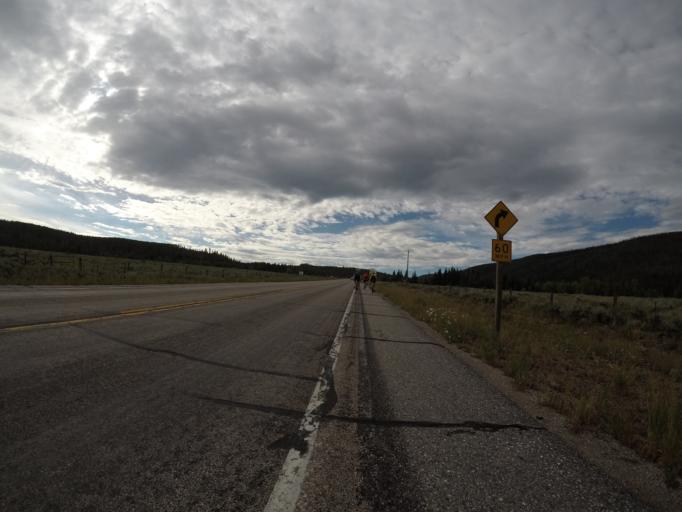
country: US
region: Wyoming
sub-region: Carbon County
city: Saratoga
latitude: 41.3481
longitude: -106.5295
